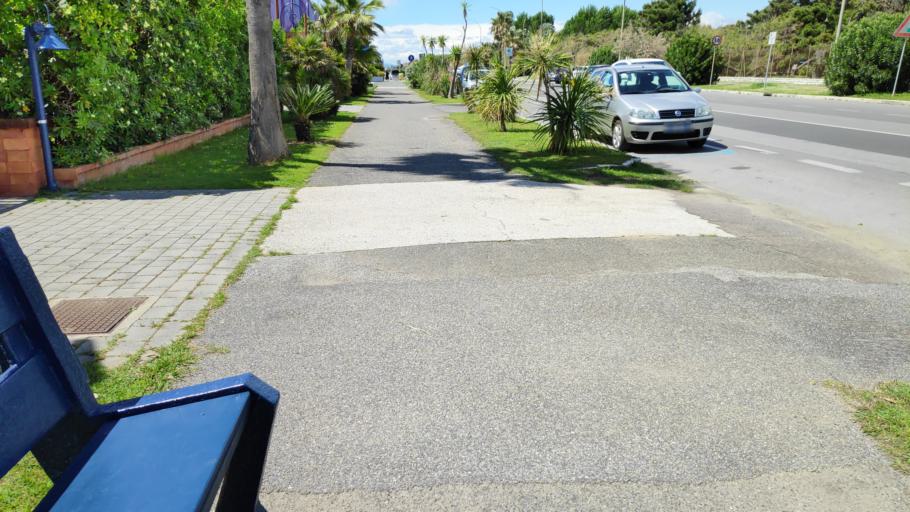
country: IT
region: Tuscany
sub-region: Provincia di Massa-Carrara
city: Massa
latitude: 43.9955
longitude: 10.1184
